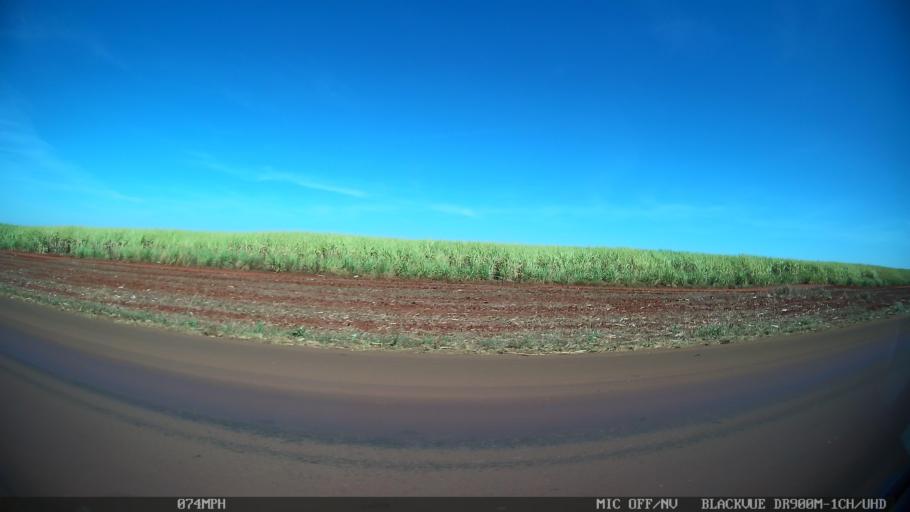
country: BR
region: Sao Paulo
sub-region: Ipua
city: Ipua
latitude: -20.4974
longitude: -47.9662
